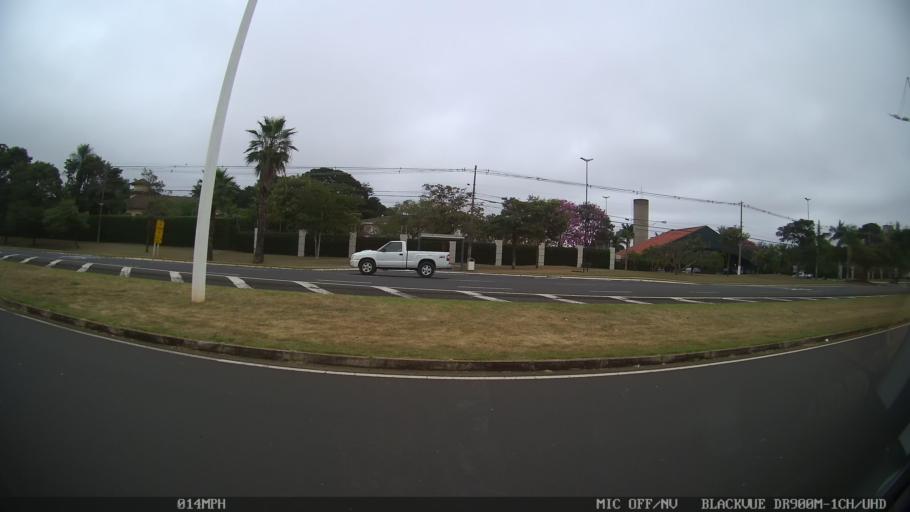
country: BR
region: Sao Paulo
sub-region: Sao Jose Do Rio Preto
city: Sao Jose do Rio Preto
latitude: -20.8517
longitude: -49.4045
